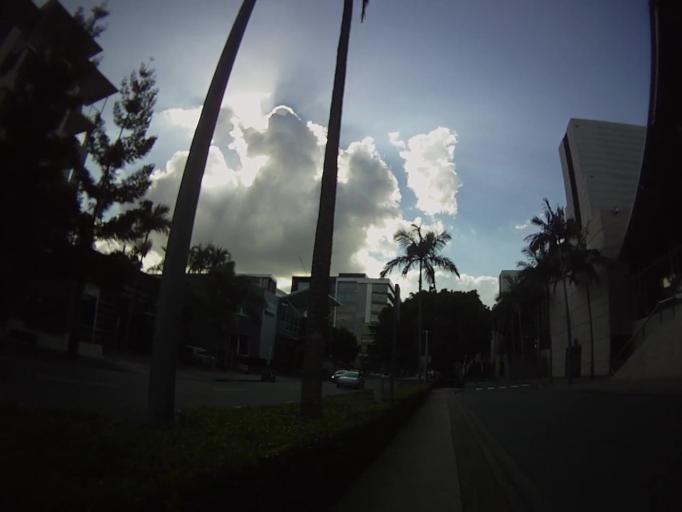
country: AU
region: Queensland
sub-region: Brisbane
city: South Brisbane
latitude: -27.4777
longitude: 153.0185
